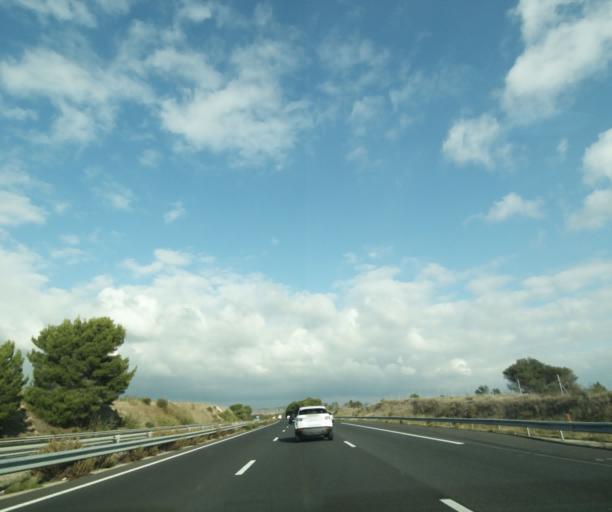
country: FR
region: Languedoc-Roussillon
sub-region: Departement de l'Aude
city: Fleury
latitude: 43.2369
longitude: 3.1410
